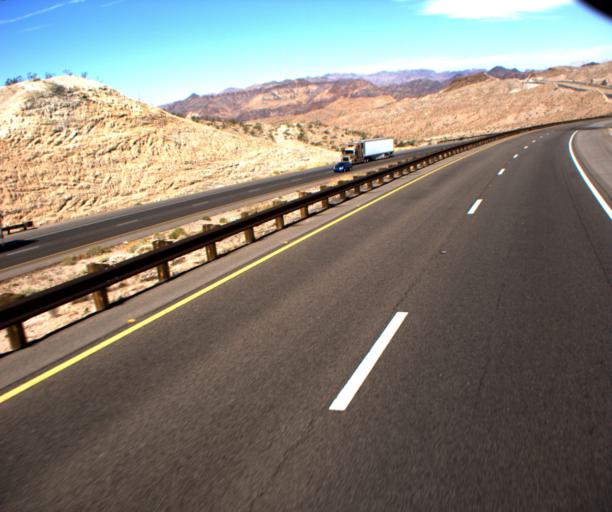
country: US
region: Nevada
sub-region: Clark County
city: Boulder City
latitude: 35.9757
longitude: -114.6941
